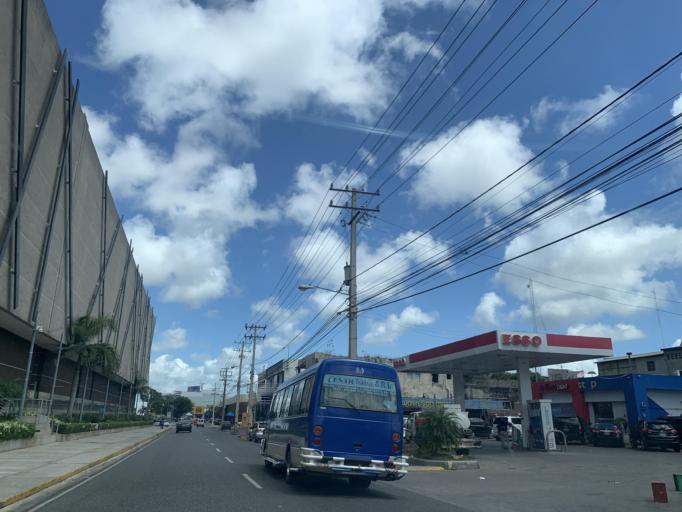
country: DO
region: Nacional
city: San Carlos
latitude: 18.4832
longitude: -69.9111
